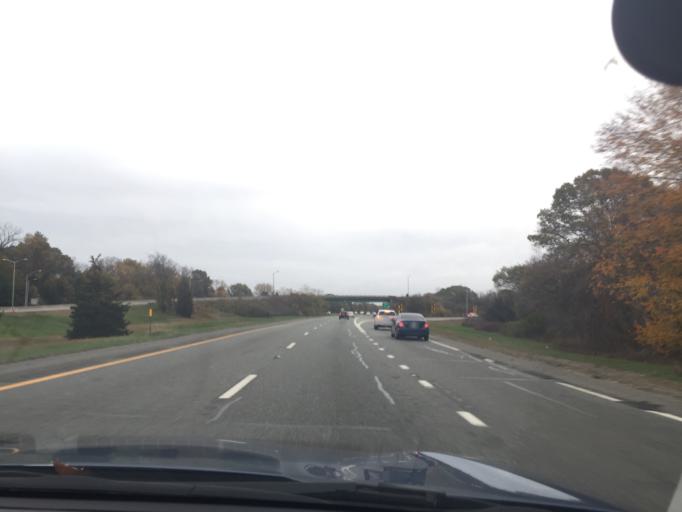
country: US
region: Rhode Island
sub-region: Providence County
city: Cranston
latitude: 41.7550
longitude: -71.4813
